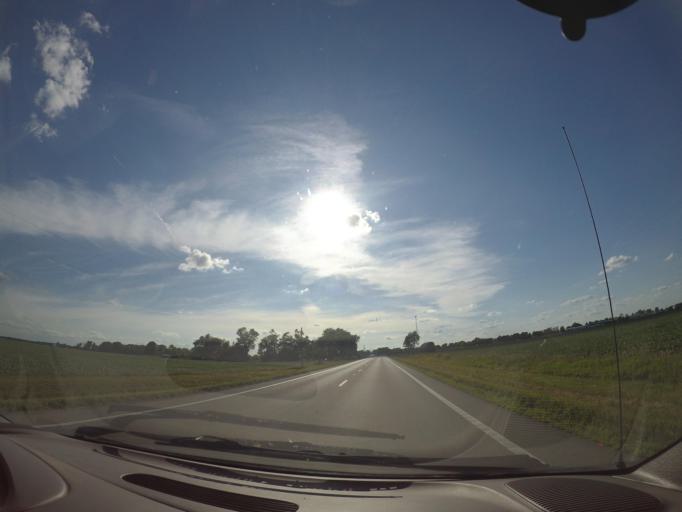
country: US
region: Ohio
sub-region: Fulton County
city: Archbold
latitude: 41.4354
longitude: -84.2415
